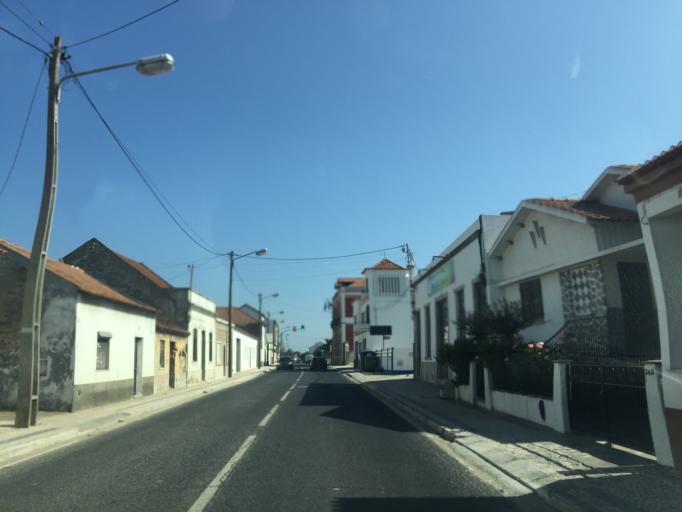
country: PT
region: Santarem
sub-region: Alpiarca
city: Alpiarca
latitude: 39.2640
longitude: -8.5801
